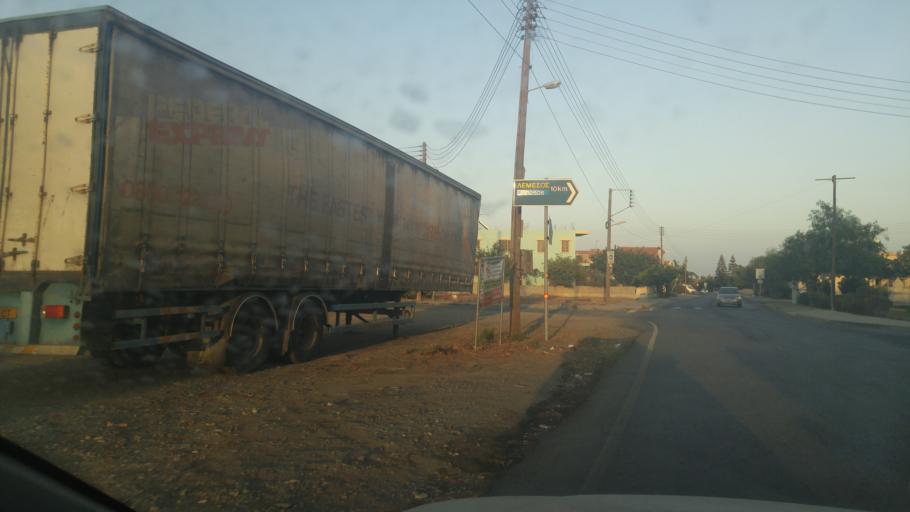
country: CY
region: Limassol
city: Ypsonas
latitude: 34.6872
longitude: 32.9732
